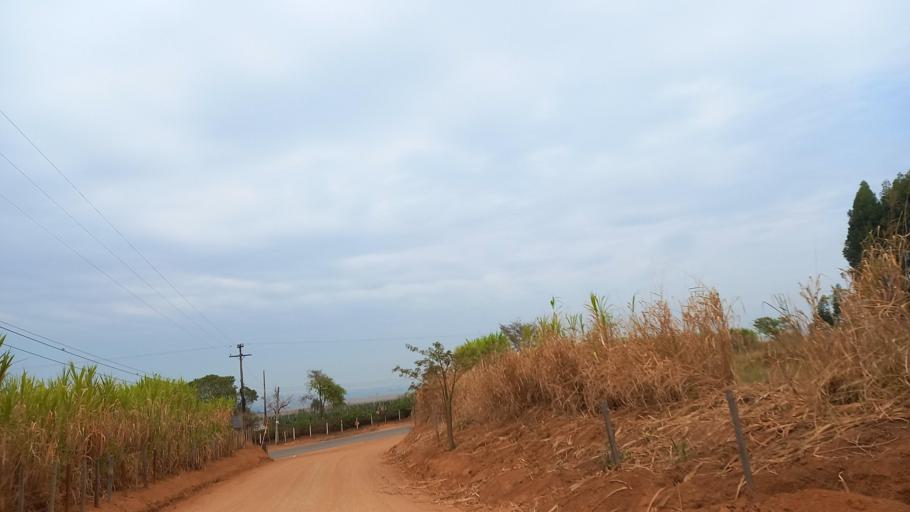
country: BR
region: Sao Paulo
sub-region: Moji-Guacu
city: Mogi-Gaucu
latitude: -22.3292
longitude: -46.8582
